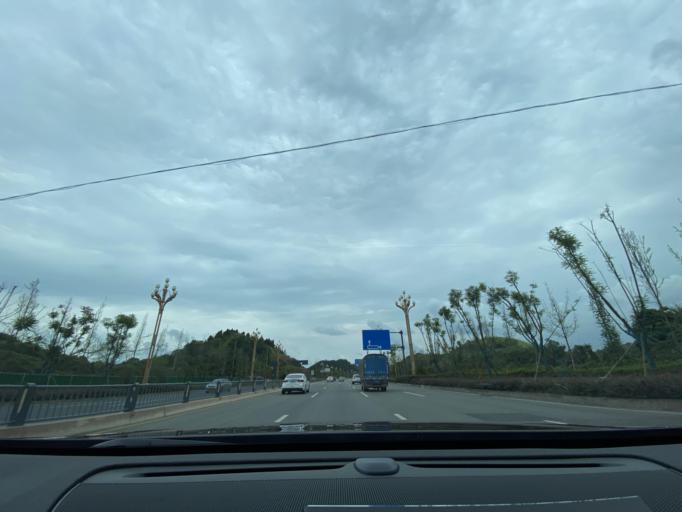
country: CN
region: Sichuan
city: Jiancheng
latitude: 30.4732
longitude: 104.4911
